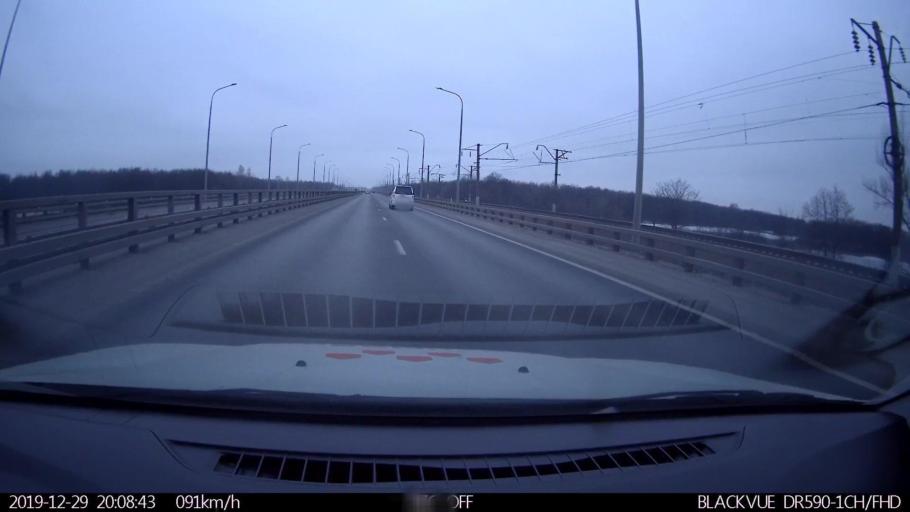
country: RU
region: Nizjnij Novgorod
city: Neklyudovo
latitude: 56.3823
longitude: 43.9610
